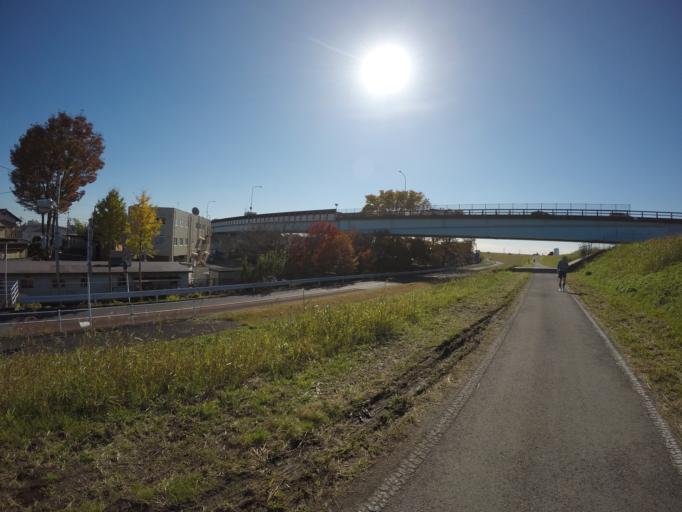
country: JP
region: Chiba
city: Matsudo
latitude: 35.7965
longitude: 139.8927
